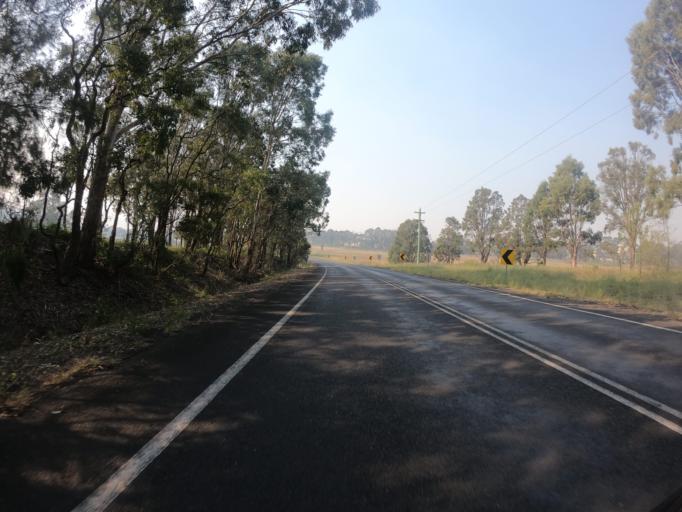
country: AU
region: New South Wales
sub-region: Wollondilly
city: Douglas Park
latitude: -34.2208
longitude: 150.7686
